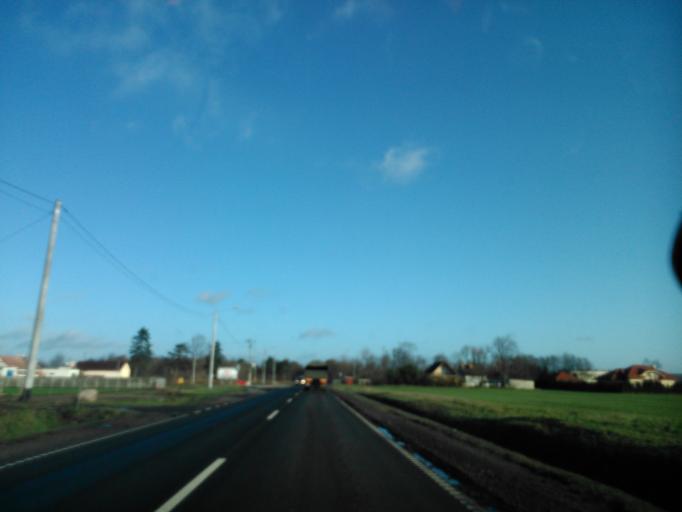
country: PL
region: Kujawsko-Pomorskie
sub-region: Powiat inowroclawski
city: Inowroclaw
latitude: 52.8238
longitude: 18.3020
